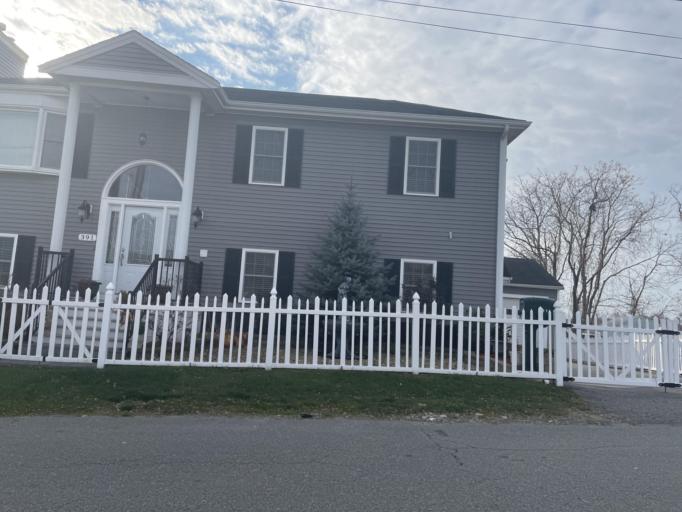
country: US
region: Massachusetts
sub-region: Bristol County
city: Fall River
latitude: 41.6830
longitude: -71.1309
